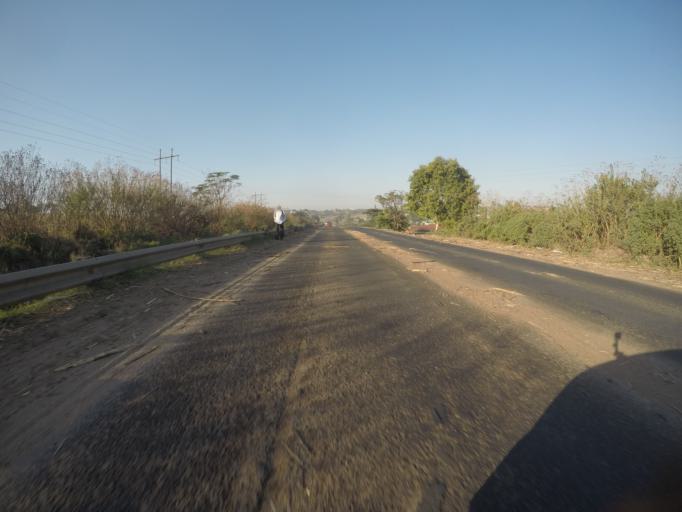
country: ZA
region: KwaZulu-Natal
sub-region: iLembe District Municipality
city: Stanger
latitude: -29.3925
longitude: 31.2512
